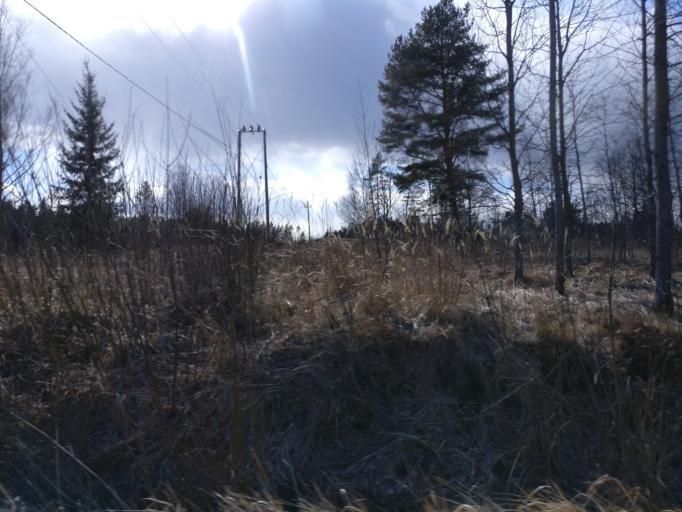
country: FI
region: Varsinais-Suomi
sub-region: Salo
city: Suomusjaervi
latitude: 60.2874
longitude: 23.6429
